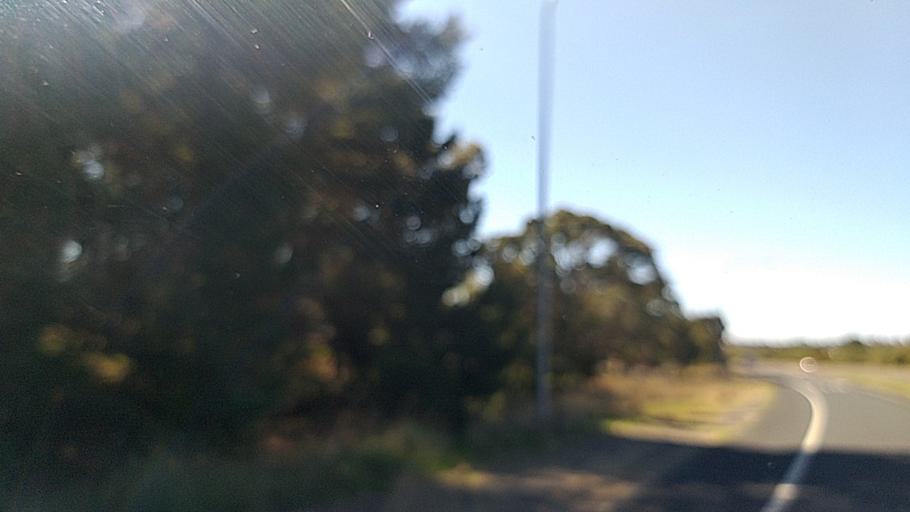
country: AU
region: Australian Capital Territory
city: Kaleen
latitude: -35.2007
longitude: 149.2124
